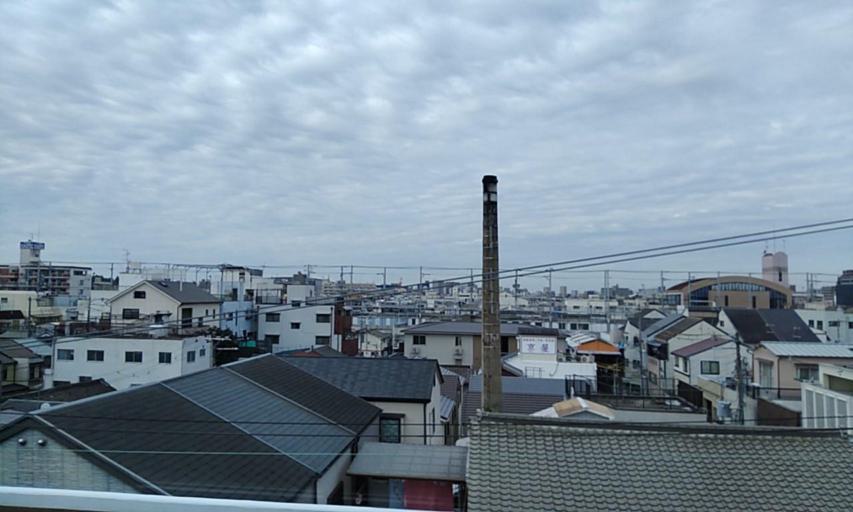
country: JP
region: Osaka
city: Matsubara
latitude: 34.6195
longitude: 135.5327
